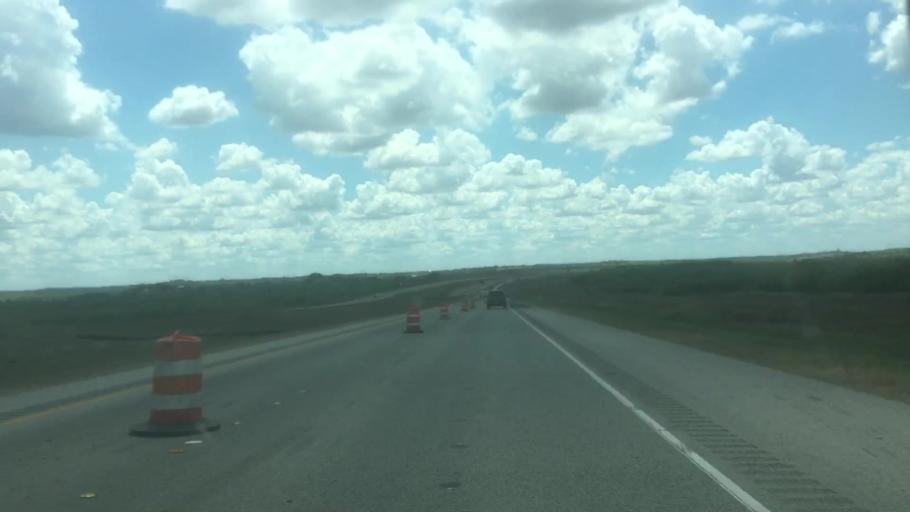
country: US
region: Texas
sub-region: Caldwell County
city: Lockhart
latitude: 29.8449
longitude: -97.7277
